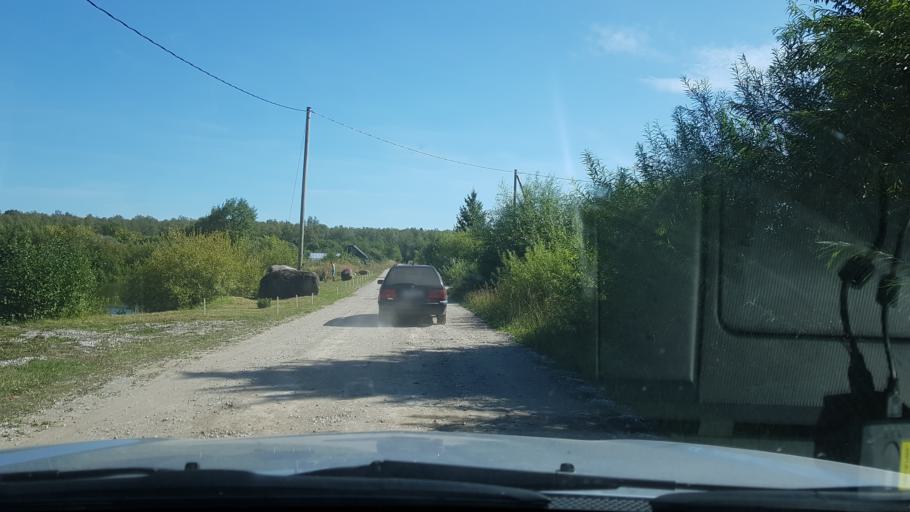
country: EE
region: Ida-Virumaa
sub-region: Sillamaee linn
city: Sillamae
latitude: 59.3720
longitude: 27.7911
